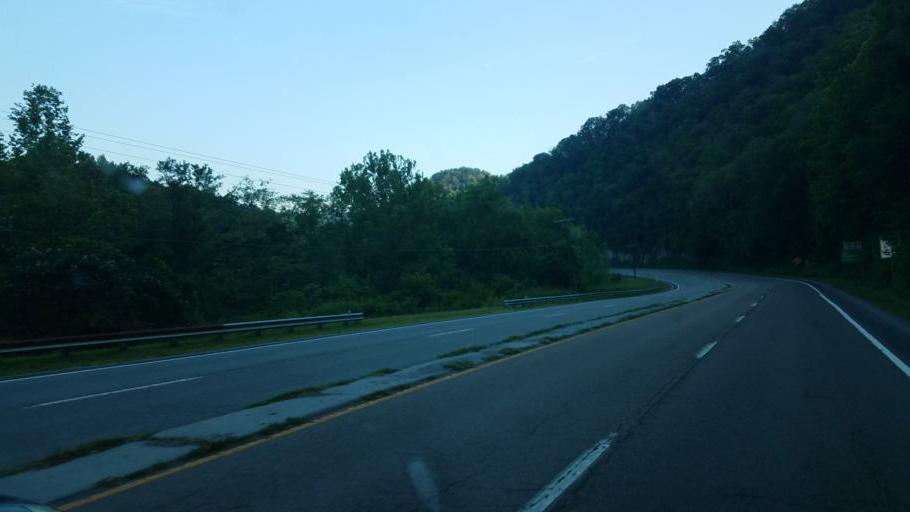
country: US
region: Tennessee
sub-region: Hawkins County
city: Church Hill
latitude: 36.6676
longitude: -82.7529
